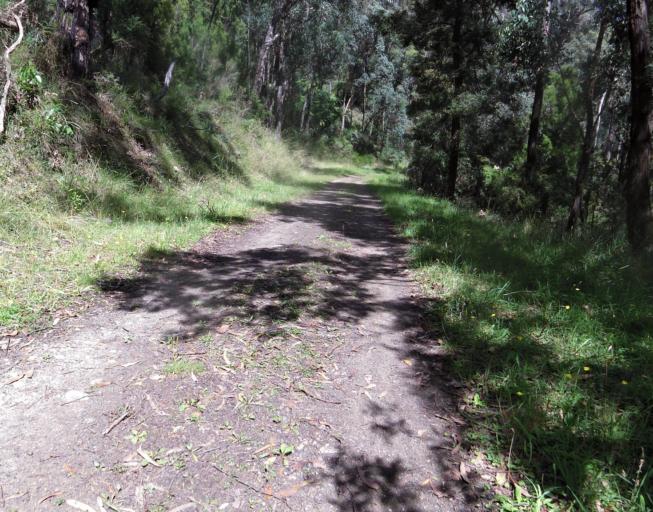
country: AU
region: Victoria
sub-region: Yarra Ranges
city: Kalorama
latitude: -37.8196
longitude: 145.3588
